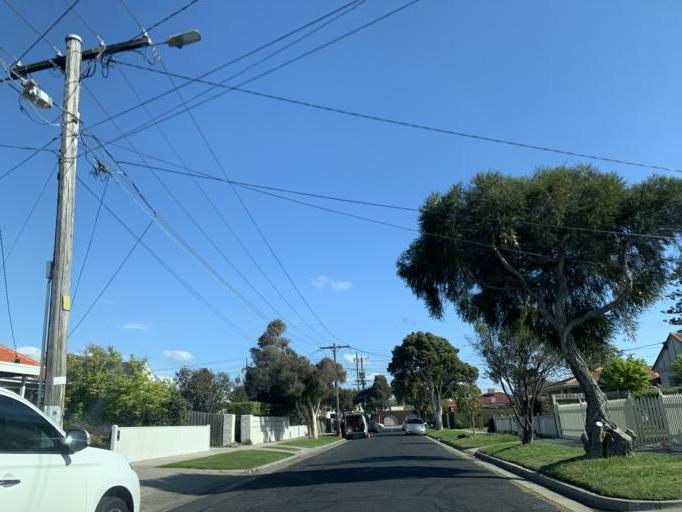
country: AU
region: Victoria
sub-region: Kingston
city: Mordialloc
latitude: -37.9976
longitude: 145.0864
